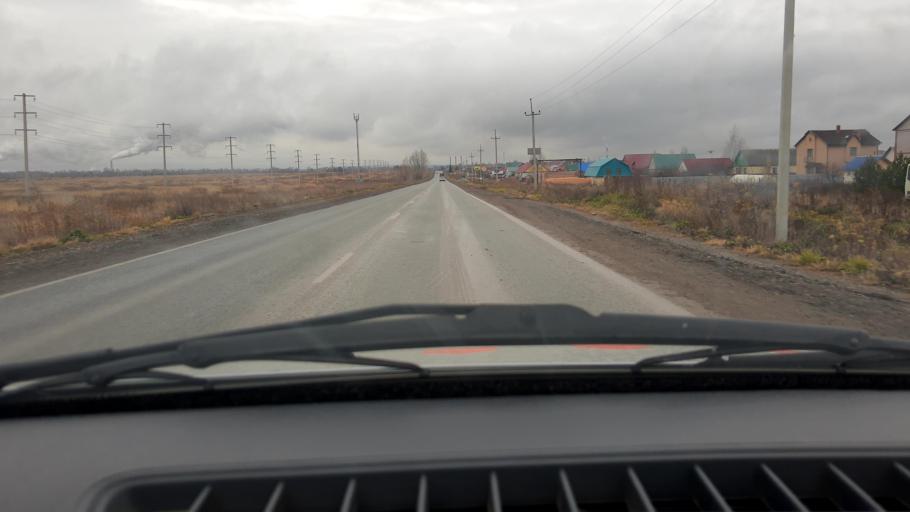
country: RU
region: Bashkortostan
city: Iglino
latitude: 54.7881
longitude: 56.2520
